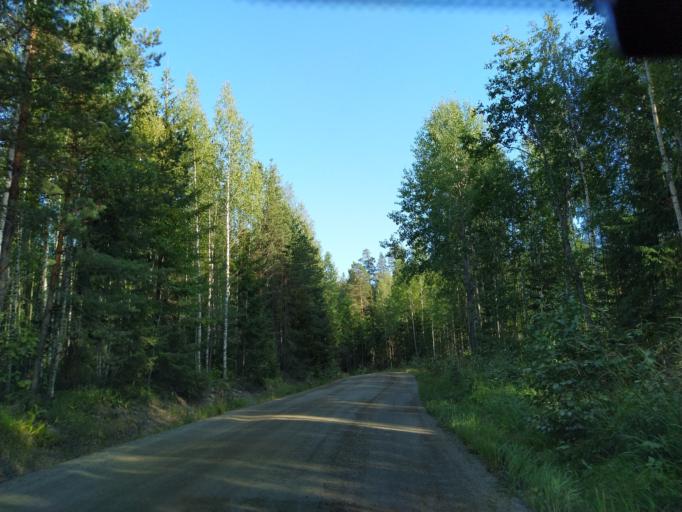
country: FI
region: Central Finland
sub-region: Jaemsae
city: Kuhmoinen
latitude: 61.6828
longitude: 24.9748
